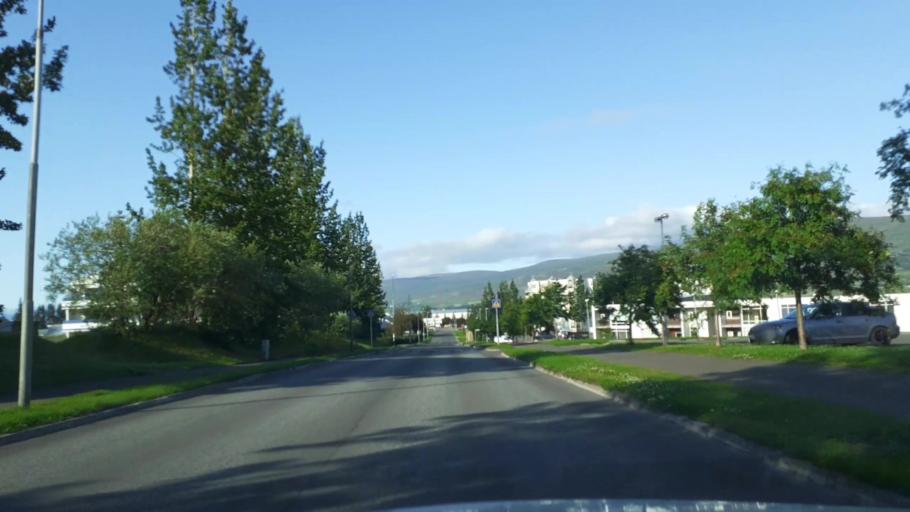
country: IS
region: Northeast
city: Akureyri
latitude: 65.6928
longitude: -18.1345
